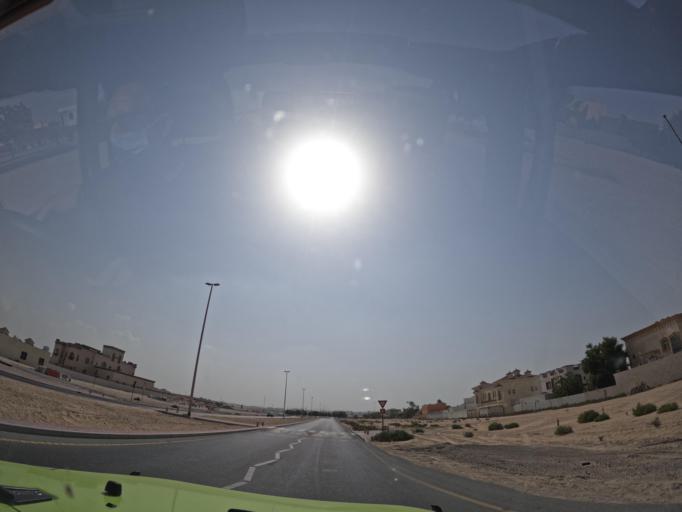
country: AE
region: Ash Shariqah
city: Sharjah
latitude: 25.1867
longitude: 55.4278
